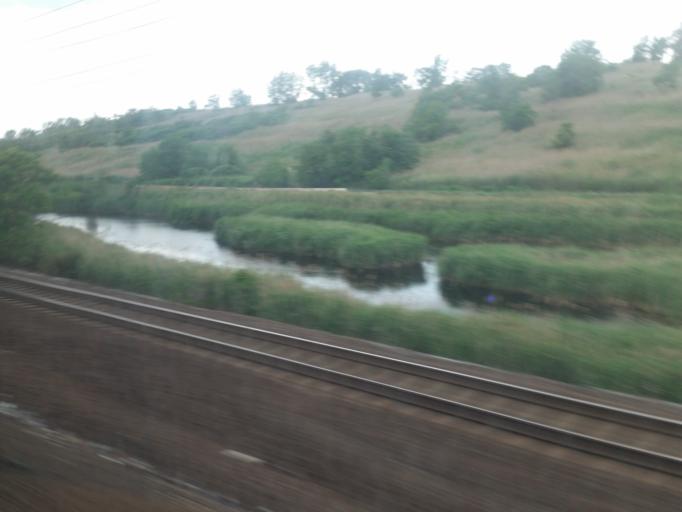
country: US
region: New Jersey
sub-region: Hudson County
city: Kearny
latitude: 40.7443
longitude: -74.1234
